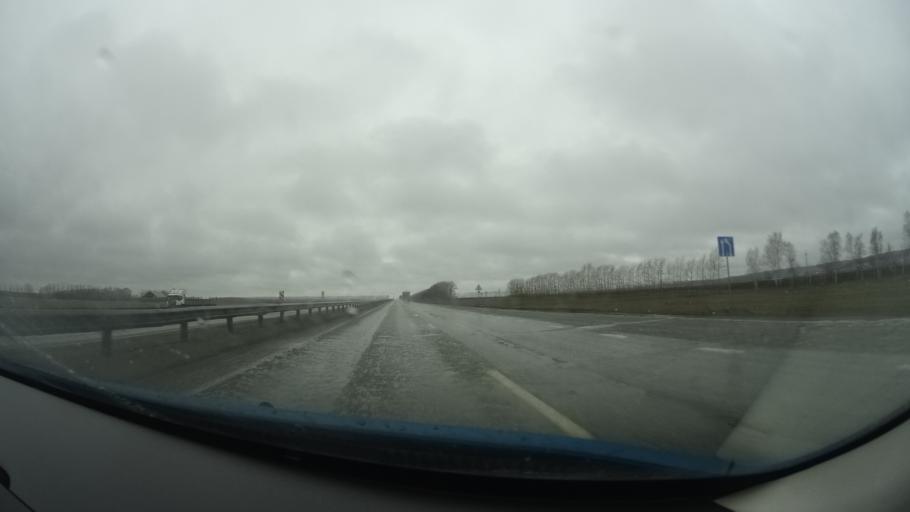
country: RU
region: Bashkortostan
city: Dmitriyevka
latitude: 54.6909
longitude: 55.2959
